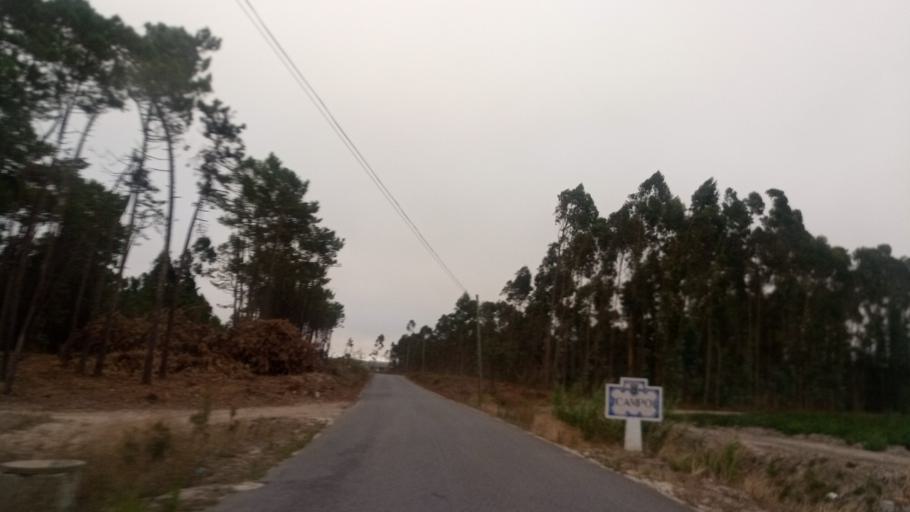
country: PT
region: Leiria
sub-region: Caldas da Rainha
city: Caldas da Rainha
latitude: 39.4425
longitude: -9.1626
